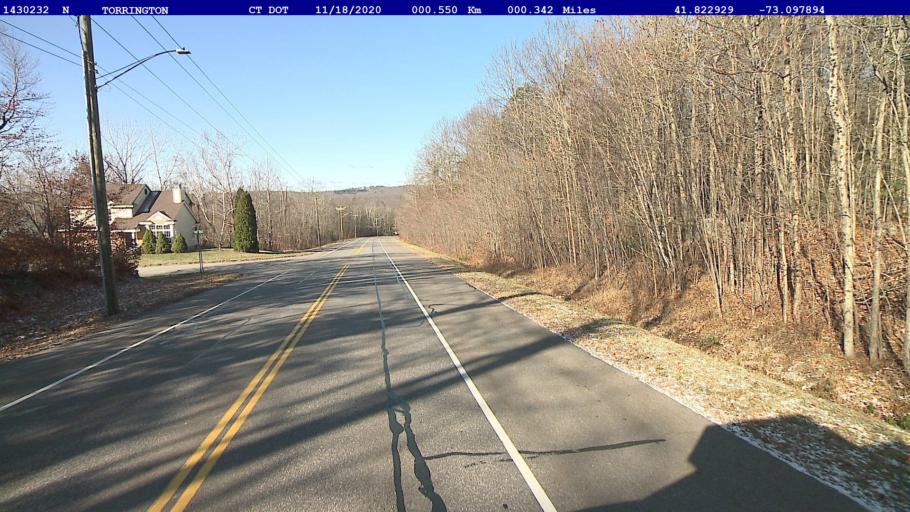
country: US
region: Connecticut
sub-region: Litchfield County
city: Torrington
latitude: 41.8229
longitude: -73.0979
